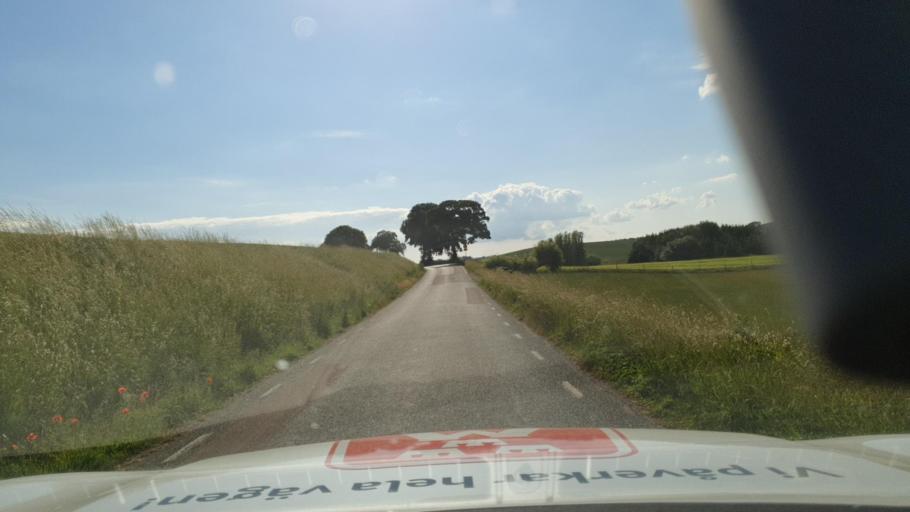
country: SE
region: Skane
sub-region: Ystads Kommun
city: Ystad
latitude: 55.4493
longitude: 13.7254
